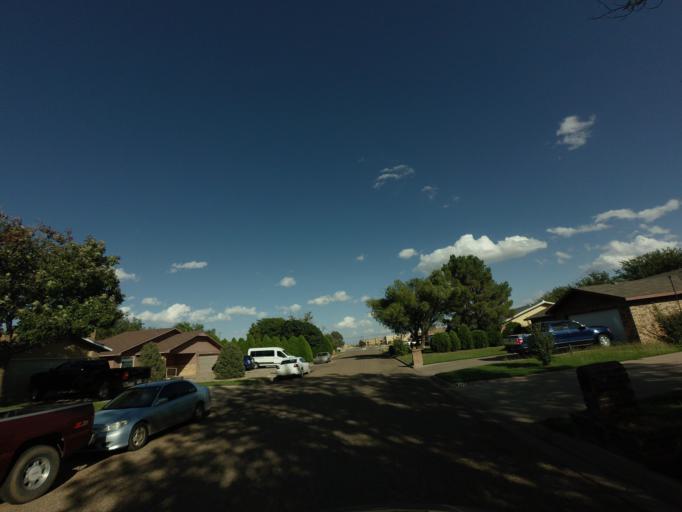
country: US
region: New Mexico
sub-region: Curry County
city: Clovis
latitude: 34.4354
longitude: -103.1798
